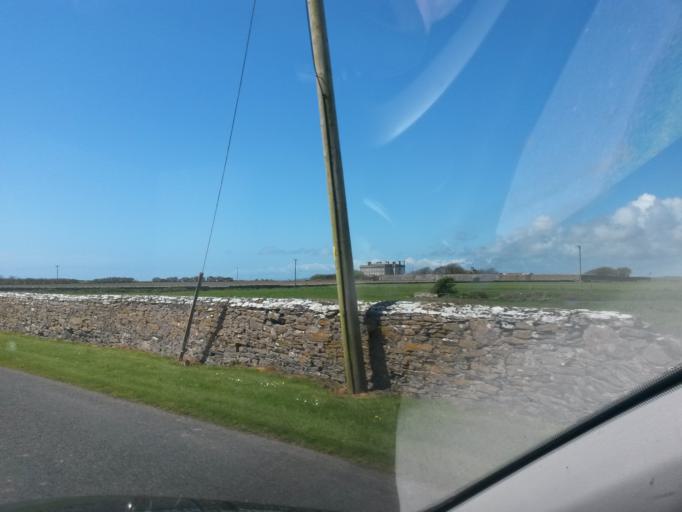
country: IE
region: Munster
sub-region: Waterford
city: Dunmore East
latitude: 52.1487
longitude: -6.9043
